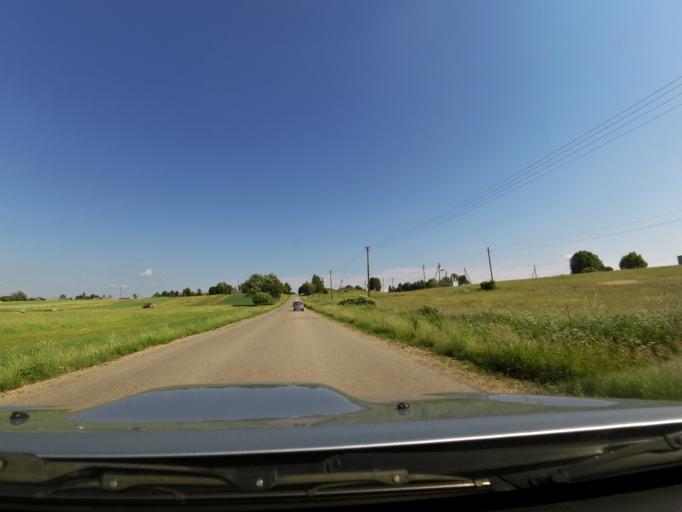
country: LT
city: Vilkaviskis
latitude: 54.5030
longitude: 23.0154
